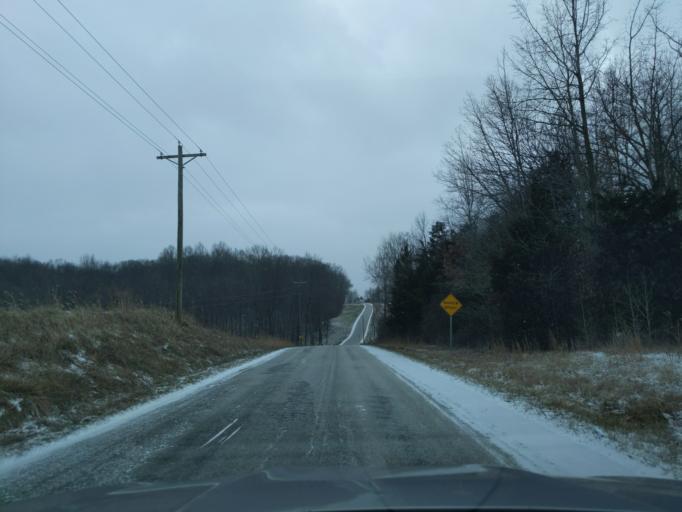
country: US
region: Indiana
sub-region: Decatur County
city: Greensburg
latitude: 39.2425
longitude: -85.4684
